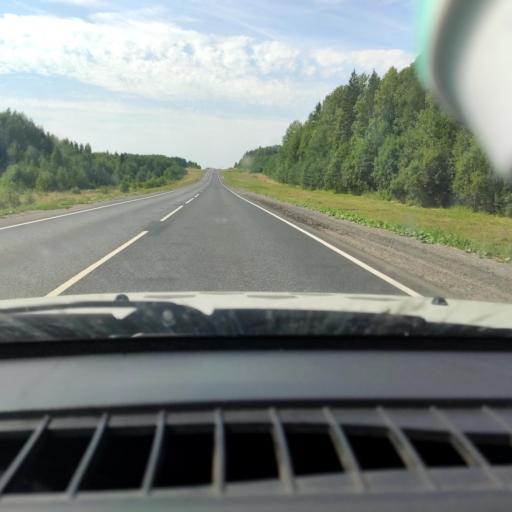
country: RU
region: Kirov
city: Kostino
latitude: 58.7302
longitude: 53.6472
